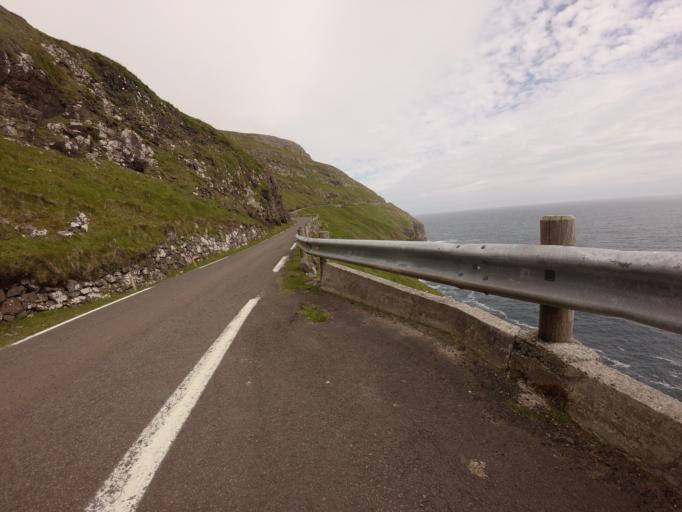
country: FO
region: Sandoy
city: Sandur
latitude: 61.7867
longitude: -6.6670
